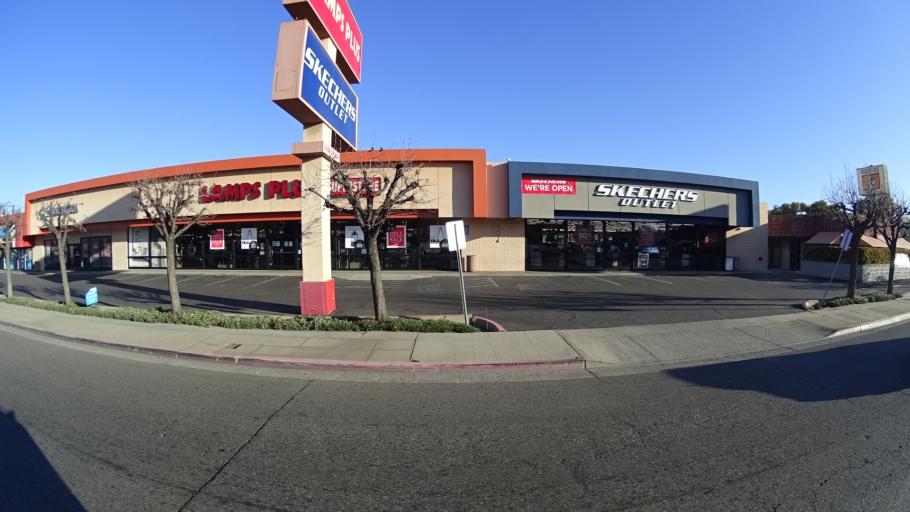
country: US
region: California
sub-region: Fresno County
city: Fresno
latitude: 36.8086
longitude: -119.7888
